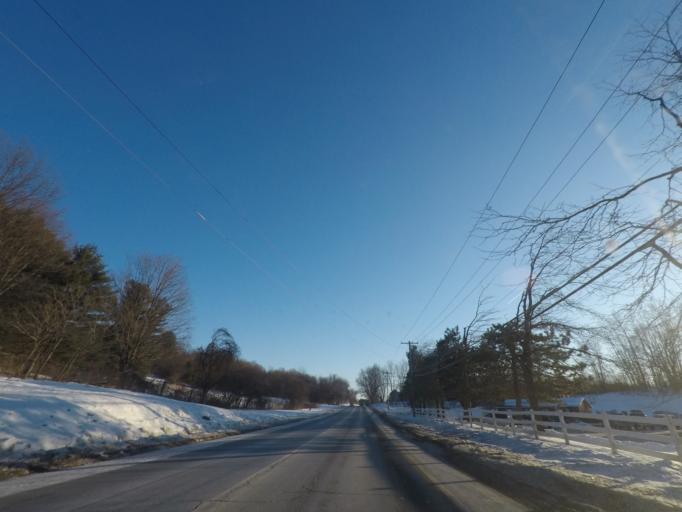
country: US
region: New York
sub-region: Saratoga County
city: Waterford
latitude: 42.8124
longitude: -73.6341
